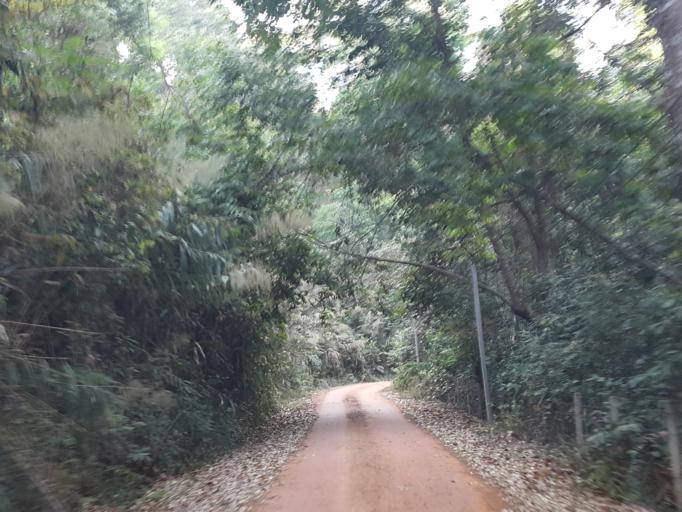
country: TH
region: Chiang Mai
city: Samoeng
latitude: 18.9038
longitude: 98.7946
